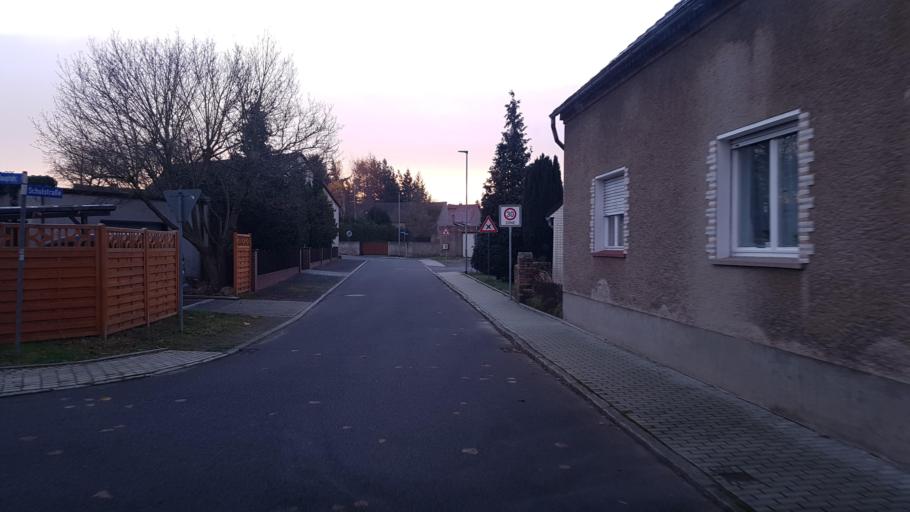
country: DE
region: Brandenburg
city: Lauchhammer
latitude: 51.5124
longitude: 13.7515
